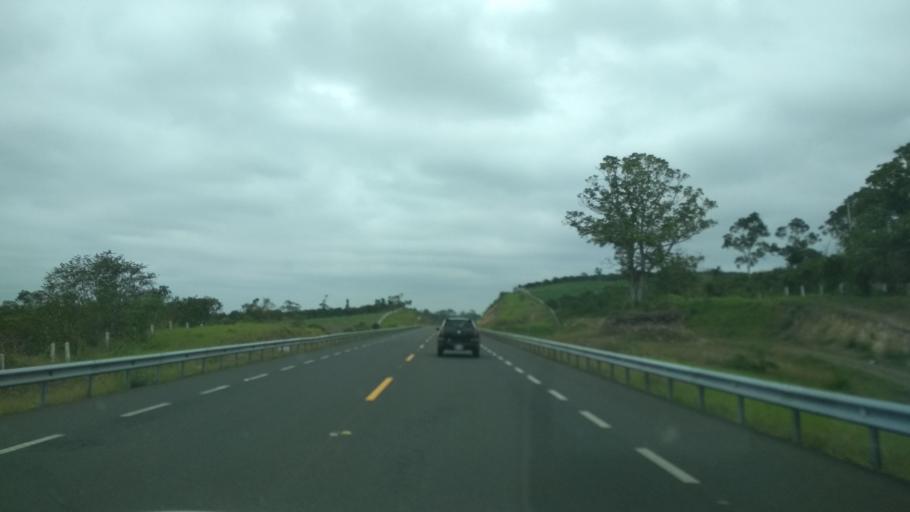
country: MX
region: Veracruz
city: Papantla de Olarte
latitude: 20.4412
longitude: -97.2359
